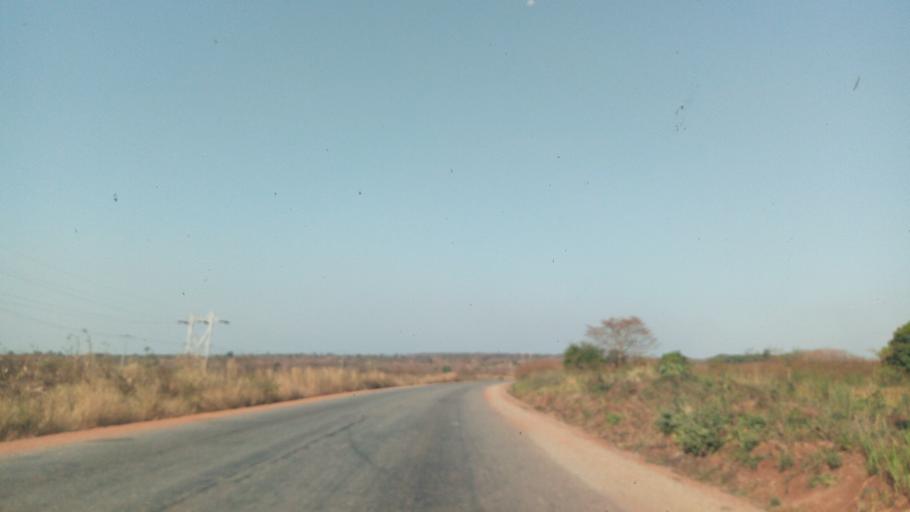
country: CD
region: Katanga
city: Likasi
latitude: -11.0001
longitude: 26.8912
